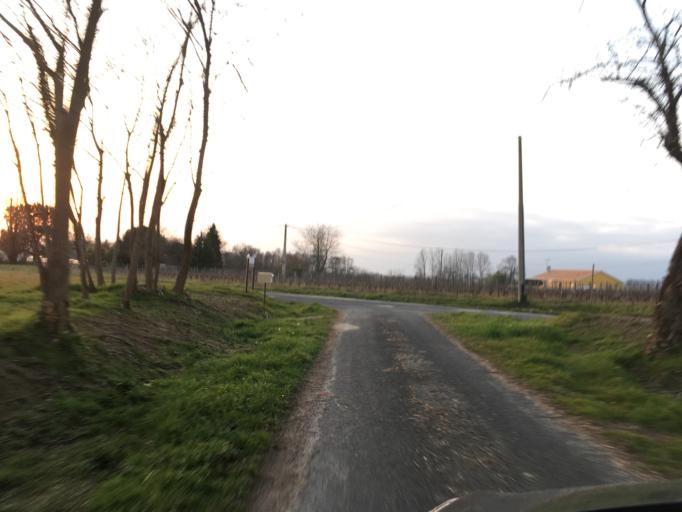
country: FR
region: Aquitaine
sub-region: Departement de la Gironde
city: Saint-Ciers-sur-Gironde
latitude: 45.2992
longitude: -0.6035
